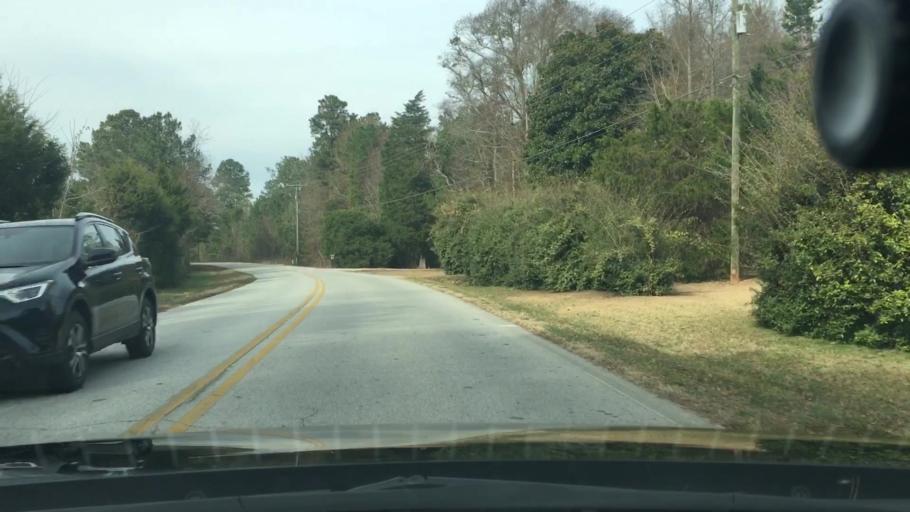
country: US
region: Georgia
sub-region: Coweta County
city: Senoia
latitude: 33.2986
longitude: -84.4611
